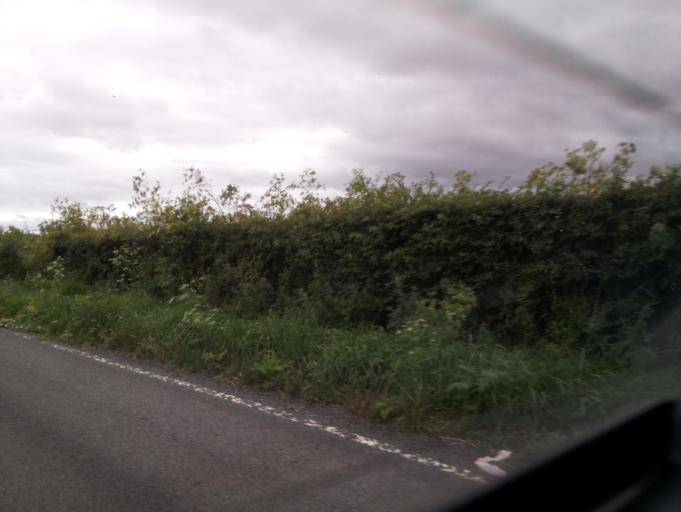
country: GB
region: England
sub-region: Worcestershire
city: Kempsey
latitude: 52.1022
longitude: -2.2149
